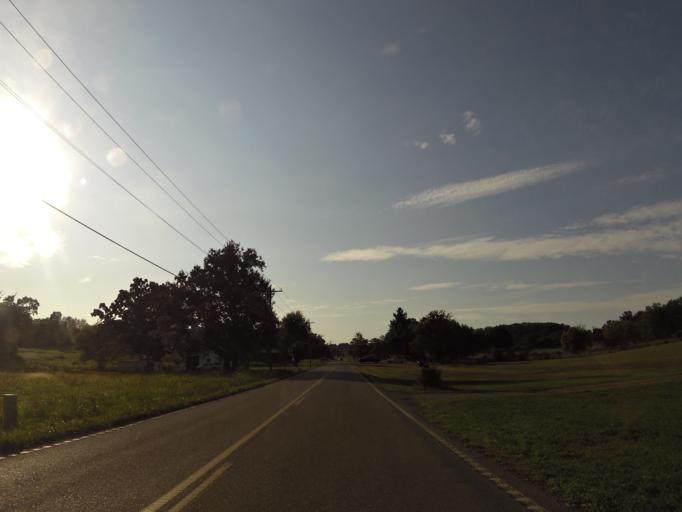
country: US
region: Tennessee
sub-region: Monroe County
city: Sweetwater
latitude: 35.6044
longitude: -84.4014
